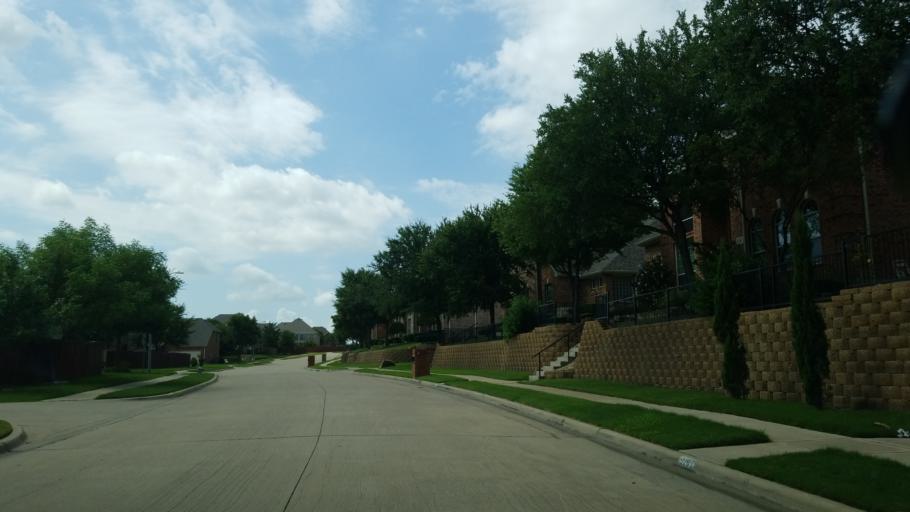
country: US
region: Texas
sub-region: Dallas County
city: Coppell
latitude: 32.9320
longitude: -96.9638
